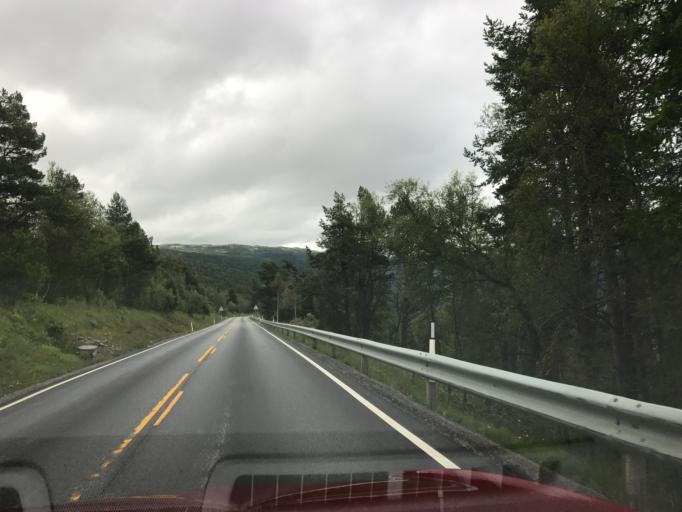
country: NO
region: Buskerud
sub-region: Al
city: Al
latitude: 60.3253
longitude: 8.5056
